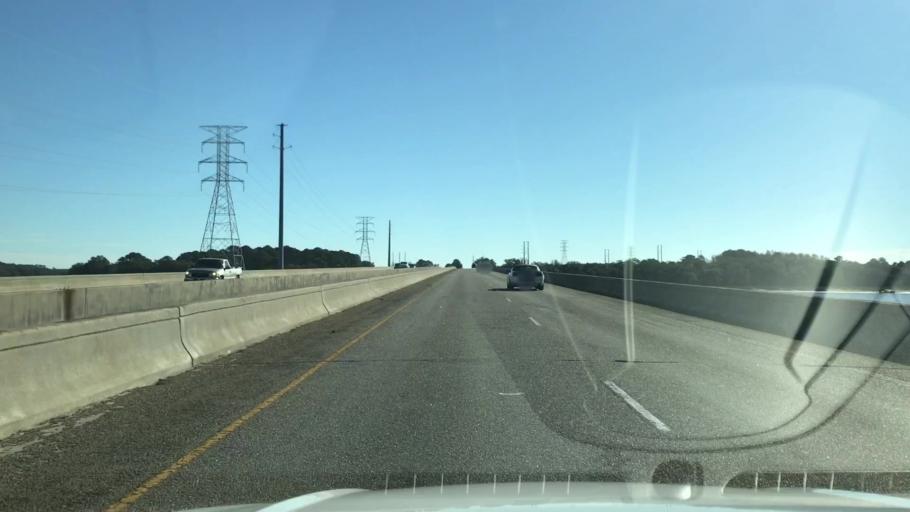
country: US
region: South Carolina
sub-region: Beaufort County
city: Hilton Head Island
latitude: 32.2308
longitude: -80.7925
